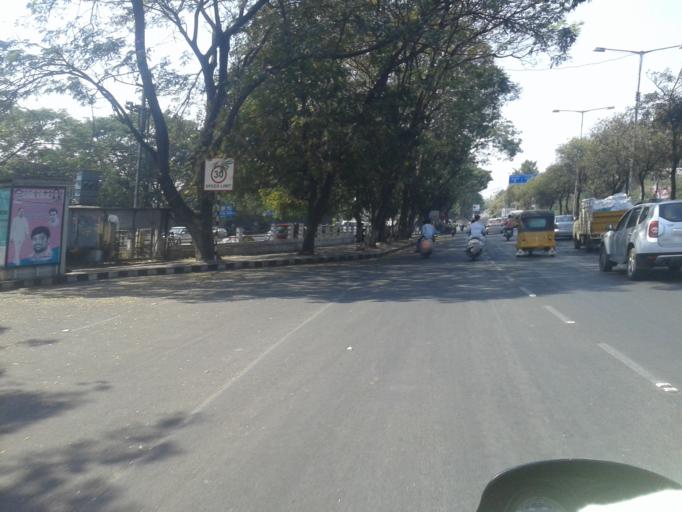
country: IN
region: Telangana
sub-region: Hyderabad
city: Hyderabad
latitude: 17.4143
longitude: 78.4676
